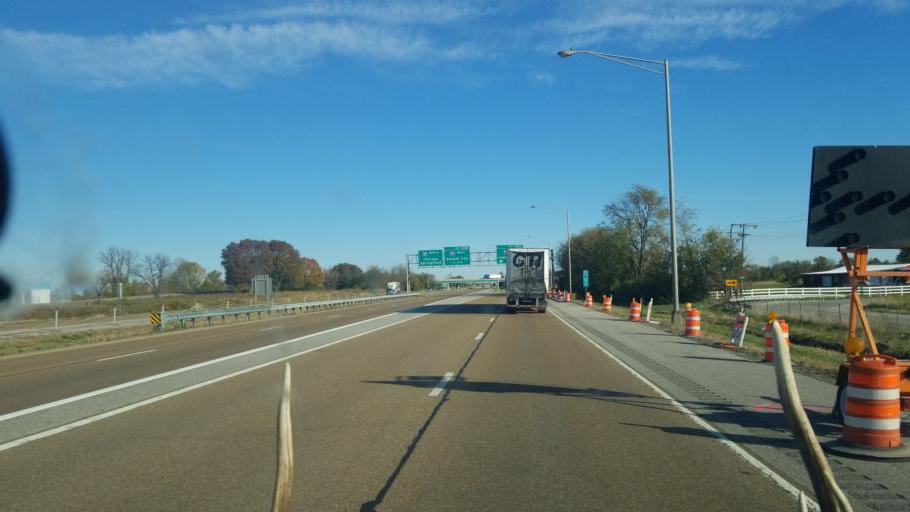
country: US
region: Illinois
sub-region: Madison County
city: Troy
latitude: 38.7439
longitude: -89.9093
